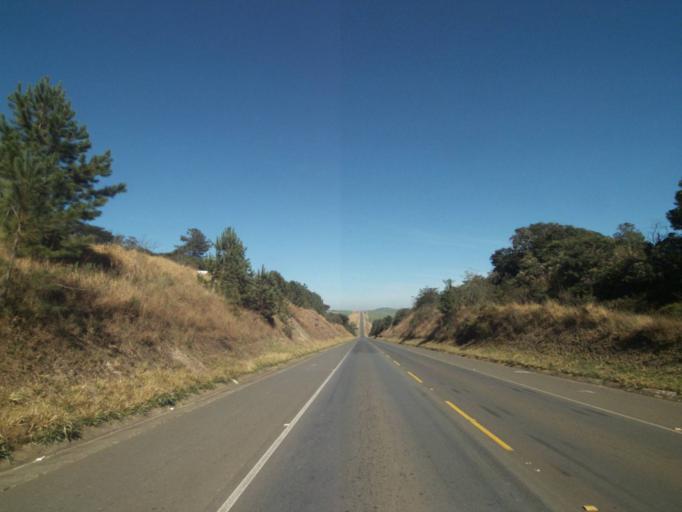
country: BR
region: Parana
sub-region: Tibagi
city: Tibagi
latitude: -24.6049
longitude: -50.4403
